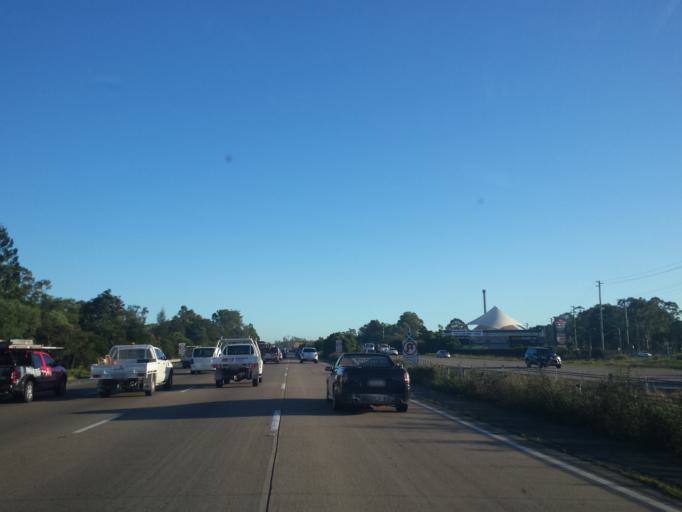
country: AU
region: Queensland
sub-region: Gold Coast
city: Oxenford
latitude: -27.8733
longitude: 153.3137
